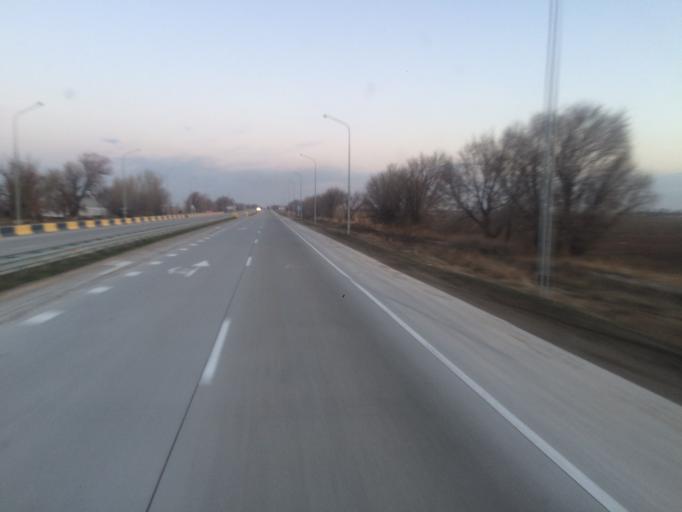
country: KZ
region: Ongtustik Qazaqstan
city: Shayan
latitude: 42.9585
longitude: 68.8913
